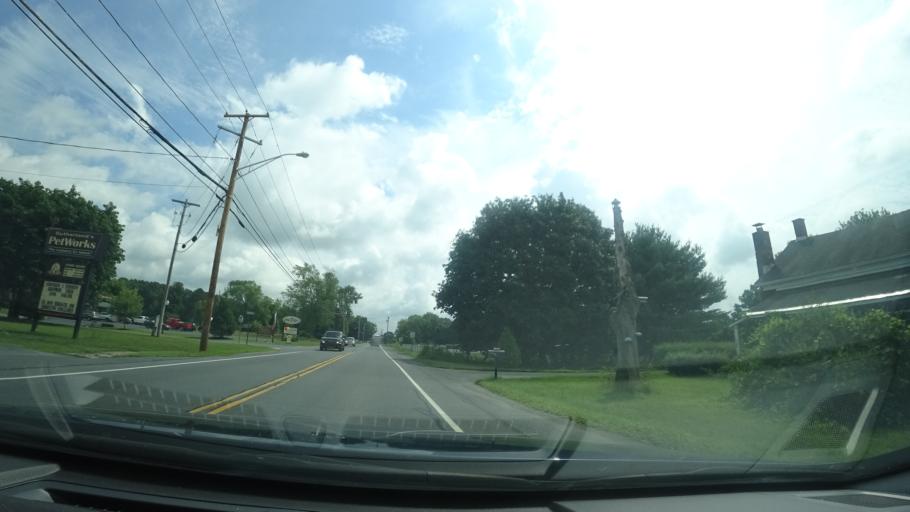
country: US
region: New York
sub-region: Washington County
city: Hudson Falls
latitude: 43.3195
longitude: -73.5826
